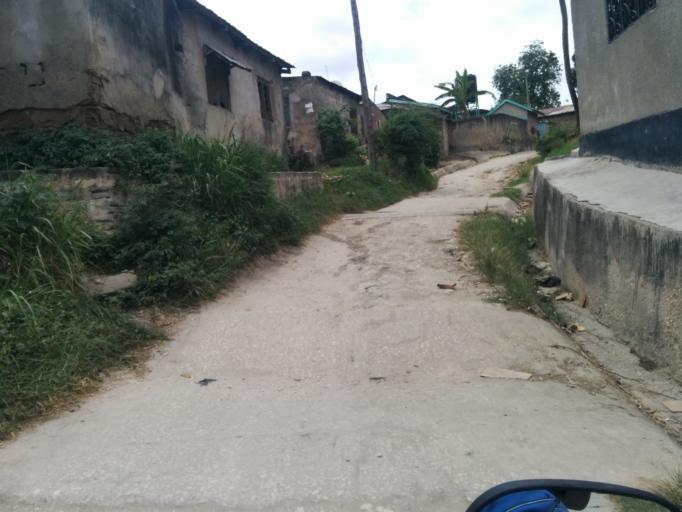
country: TZ
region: Dar es Salaam
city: Dar es Salaam
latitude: -6.8633
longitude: 39.2482
